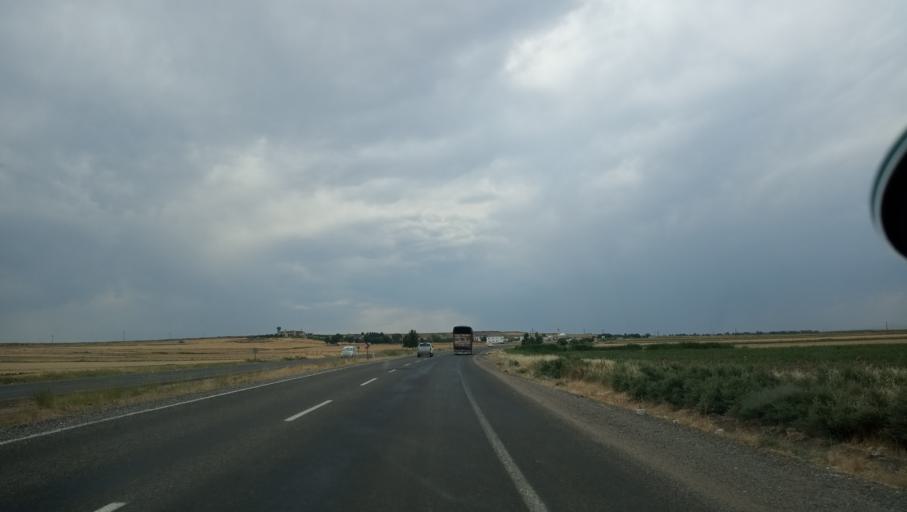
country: TR
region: Diyarbakir
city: Cinar
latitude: 37.8045
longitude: 40.3748
